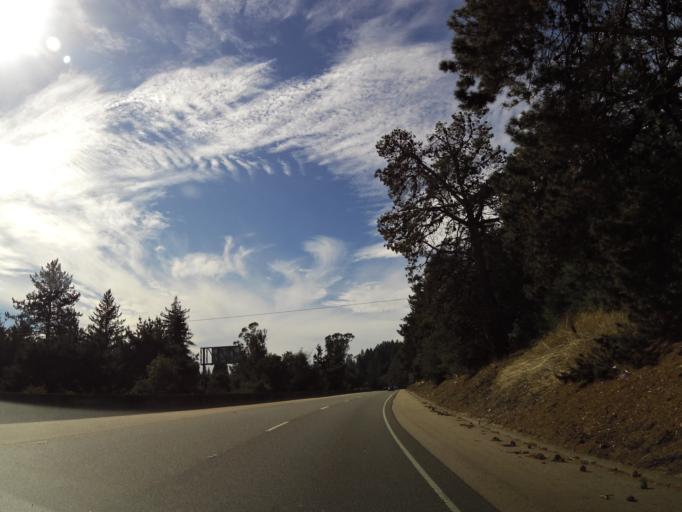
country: US
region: California
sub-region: Santa Cruz County
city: Pasatiempo
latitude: 37.0284
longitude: -122.0236
